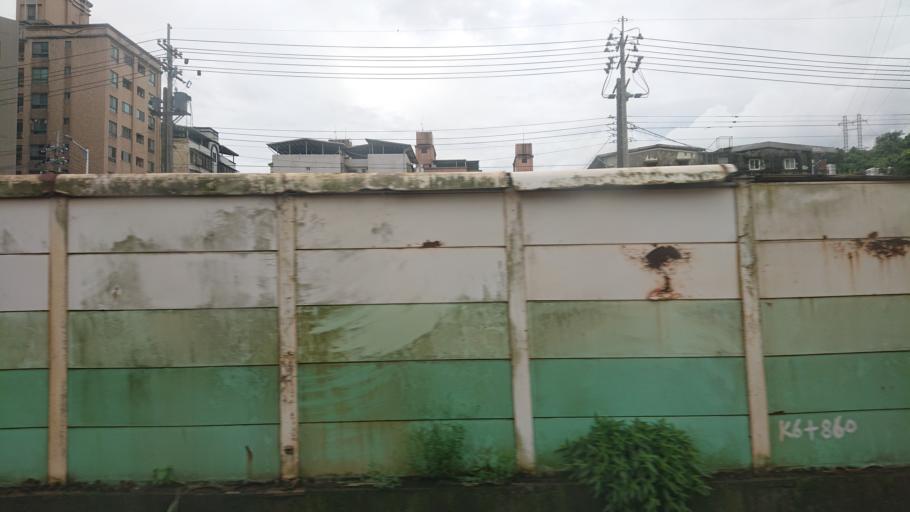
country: TW
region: Taiwan
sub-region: Keelung
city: Keelung
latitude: 25.0890
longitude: 121.7070
